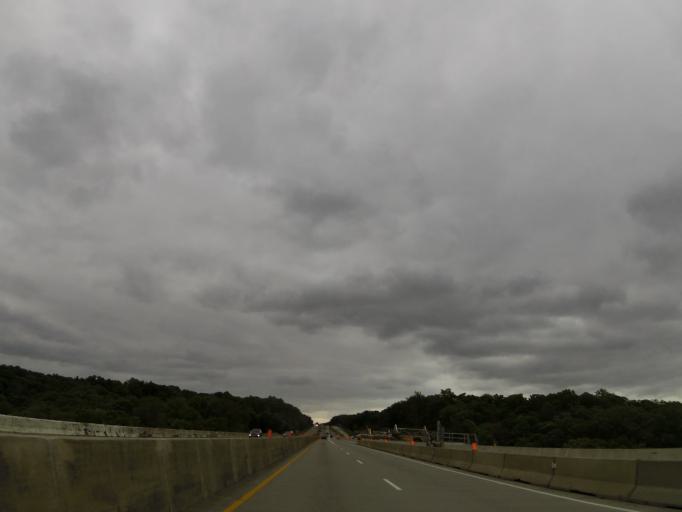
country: US
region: Ohio
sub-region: Warren County
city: Morrow
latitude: 39.4200
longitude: -84.1028
